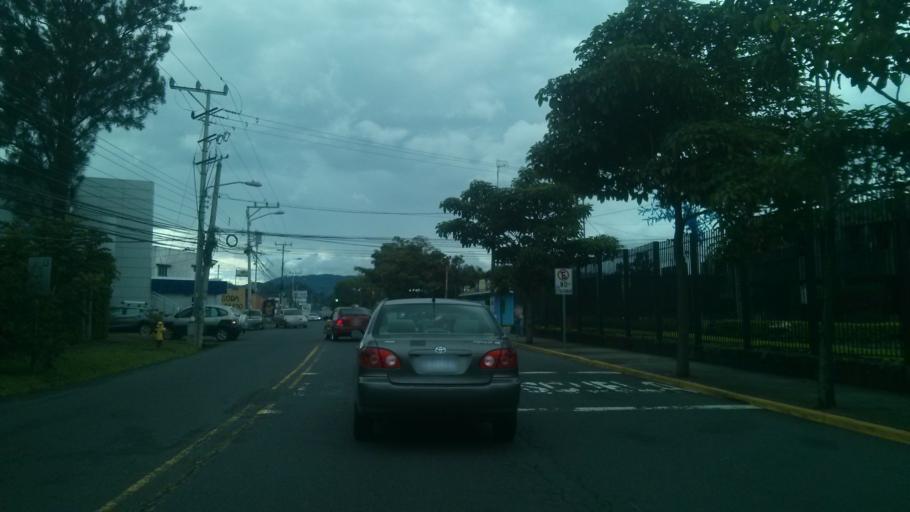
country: CR
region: San Jose
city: San Pedro
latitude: 9.9234
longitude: -84.0556
